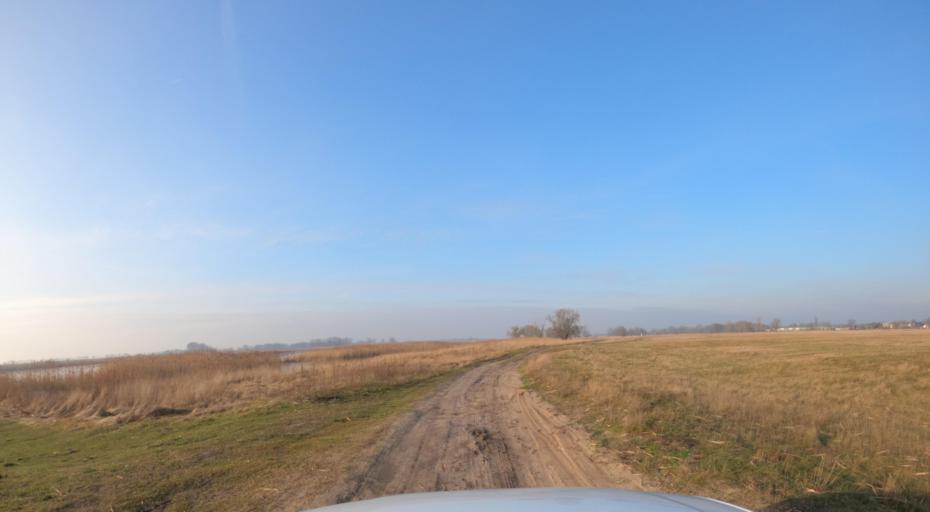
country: PL
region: Lubusz
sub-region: Powiat gorzowski
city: Kostrzyn nad Odra
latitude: 52.6146
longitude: 14.5898
